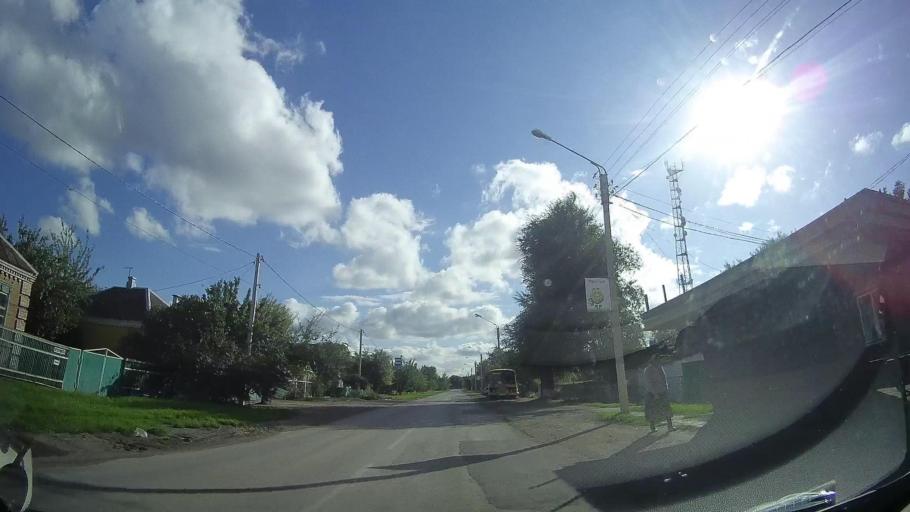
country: RU
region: Rostov
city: Tselina
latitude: 46.5337
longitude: 41.0337
